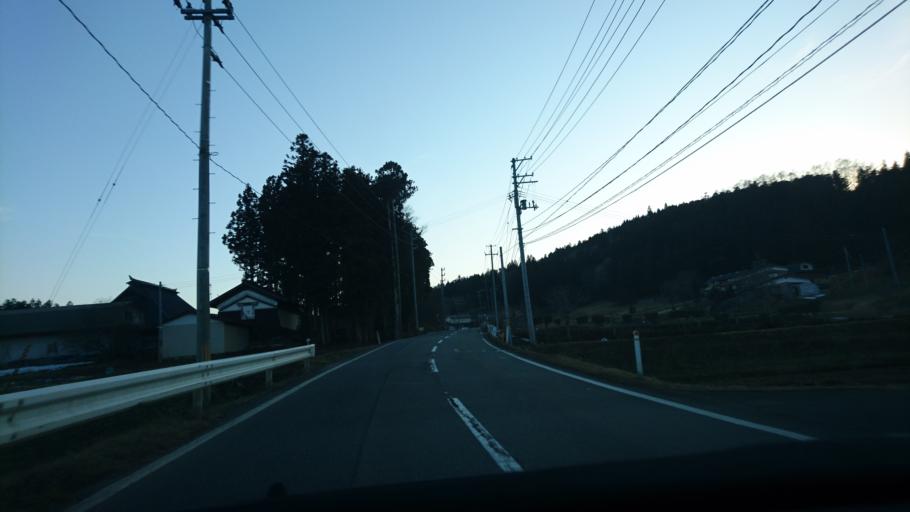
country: JP
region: Iwate
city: Ichinoseki
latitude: 39.0141
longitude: 141.2890
